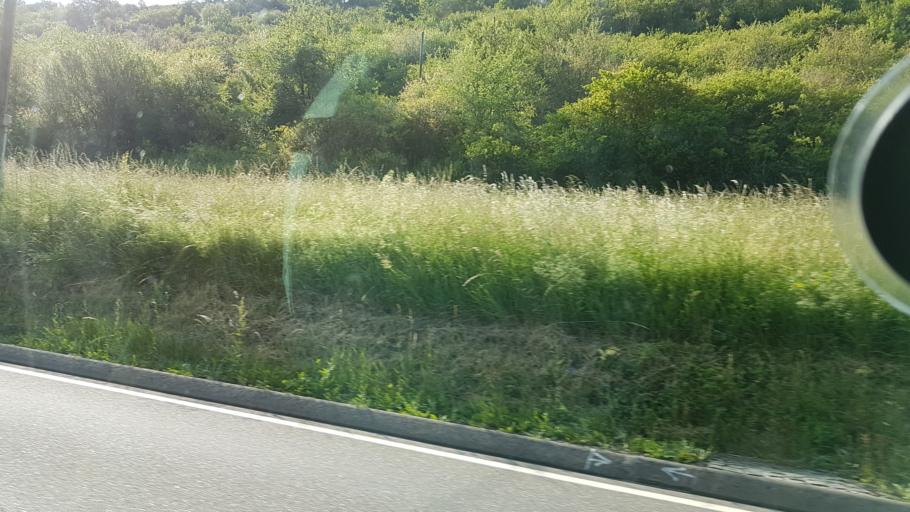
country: DE
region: Rheinland-Pfalz
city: Obermoschel
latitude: 49.7242
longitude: 7.7648
